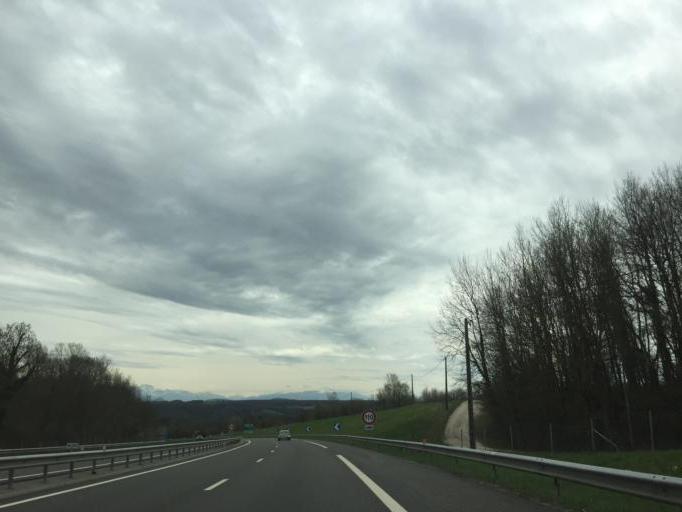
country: FR
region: Rhone-Alpes
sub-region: Departement de l'Ain
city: Bellegarde-sur-Valserine
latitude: 46.1114
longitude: 5.7982
